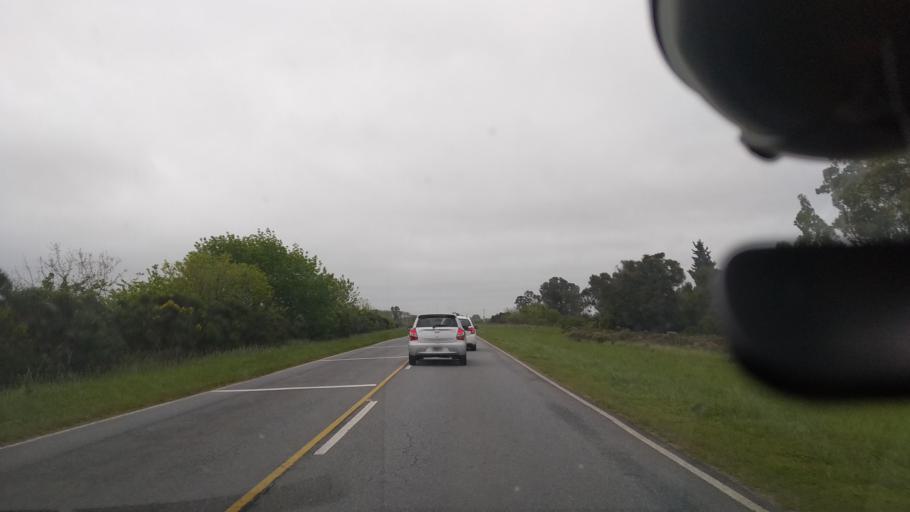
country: AR
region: Buenos Aires
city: Veronica
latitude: -35.3987
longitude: -57.3548
